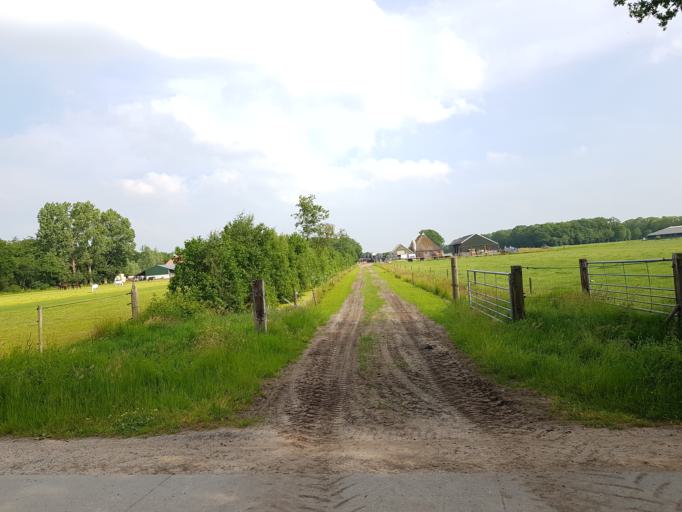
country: NL
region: Friesland
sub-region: Gemeente Heerenveen
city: Jubbega
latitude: 53.0317
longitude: 6.1080
